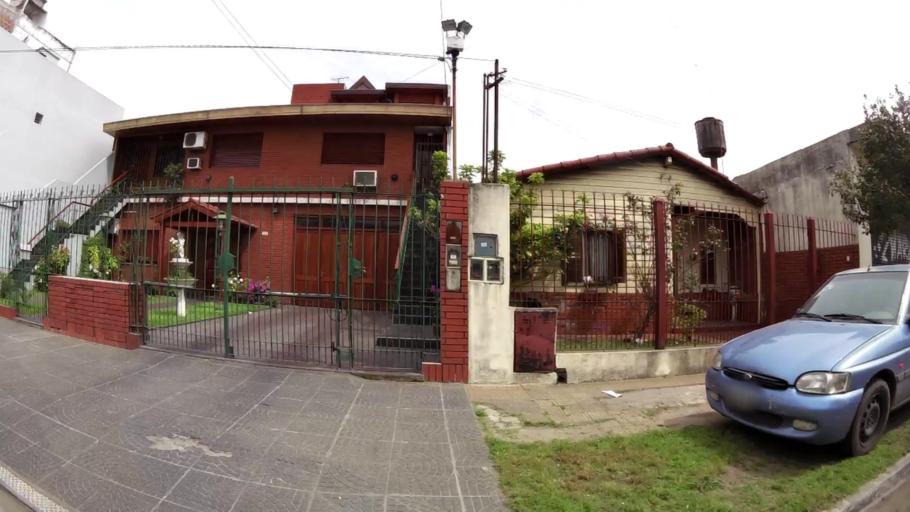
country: AR
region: Buenos Aires F.D.
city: Villa Lugano
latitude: -34.6916
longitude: -58.5095
